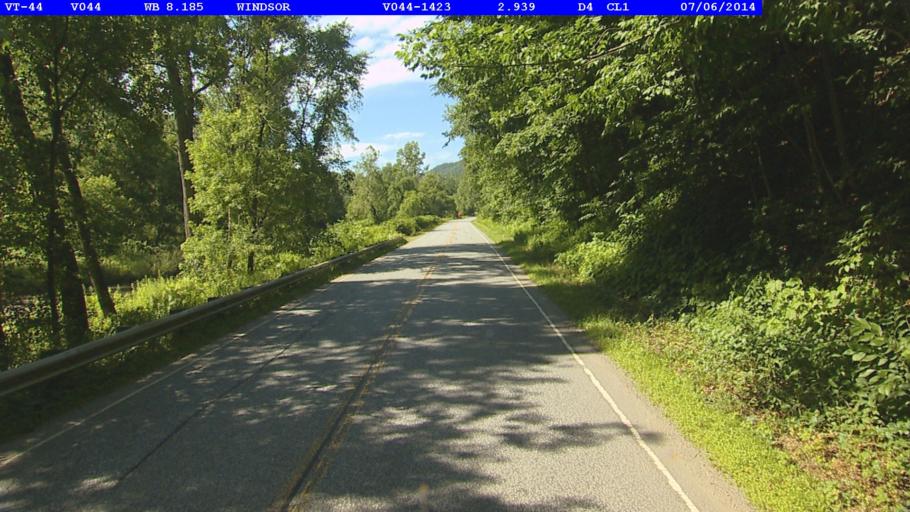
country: US
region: Vermont
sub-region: Windsor County
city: Windsor
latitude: 43.4585
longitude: -72.4044
